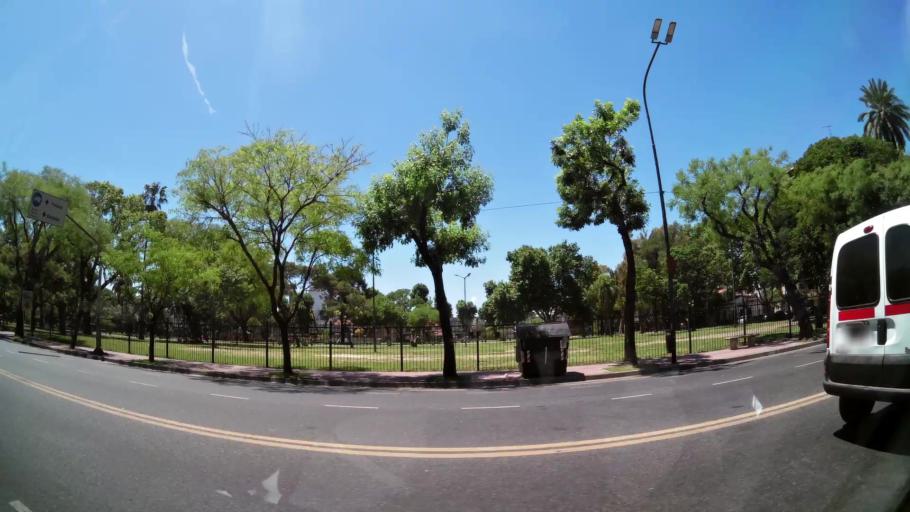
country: AR
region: Buenos Aires
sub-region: Partido de Avellaneda
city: Avellaneda
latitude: -34.6521
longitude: -58.3889
